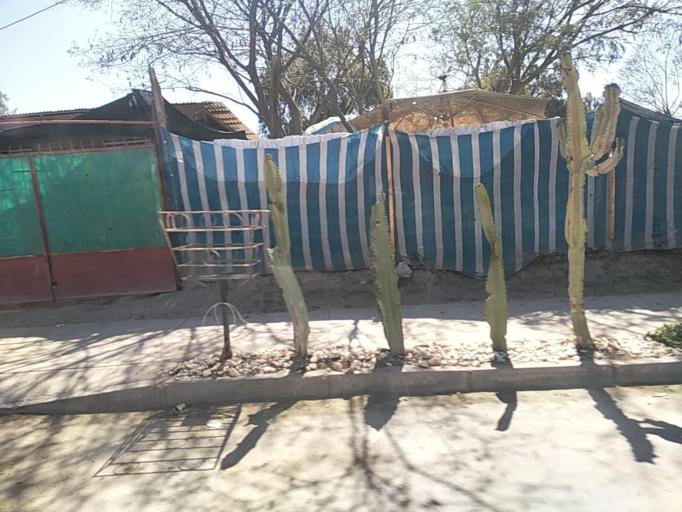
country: CL
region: Atacama
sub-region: Provincia de Copiapo
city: Copiapo
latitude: -27.4104
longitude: -70.2855
